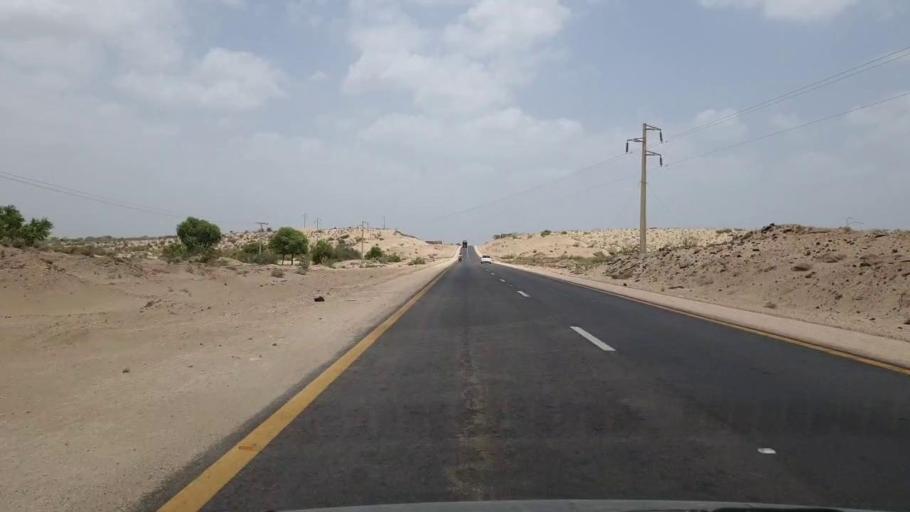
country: PK
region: Sindh
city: Naukot
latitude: 24.8382
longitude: 69.4634
